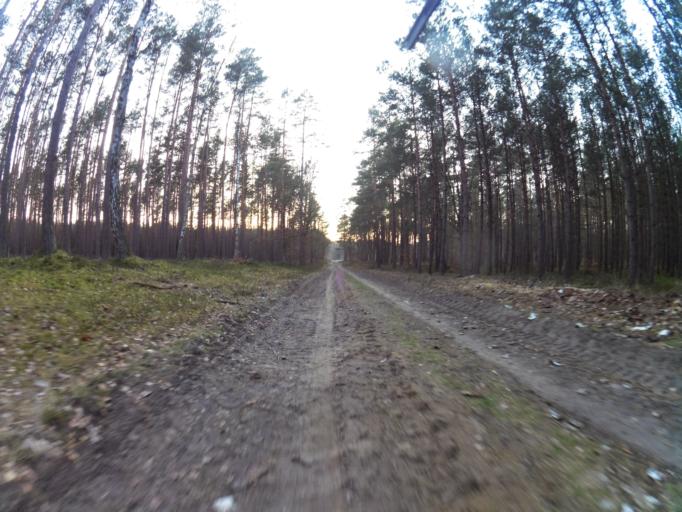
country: PL
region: West Pomeranian Voivodeship
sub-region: Powiat policki
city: Nowe Warpno
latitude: 53.6955
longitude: 14.3226
